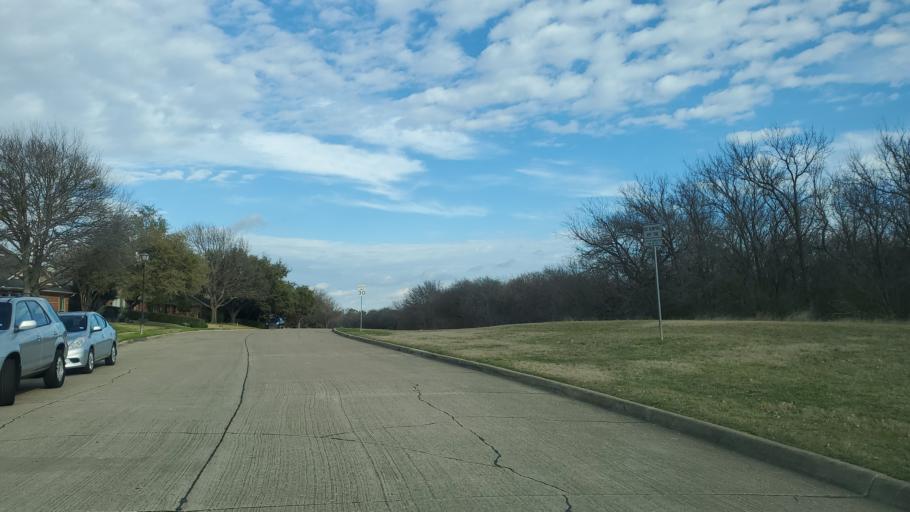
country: US
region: Texas
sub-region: Dallas County
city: Carrollton
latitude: 32.9925
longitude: -96.9009
